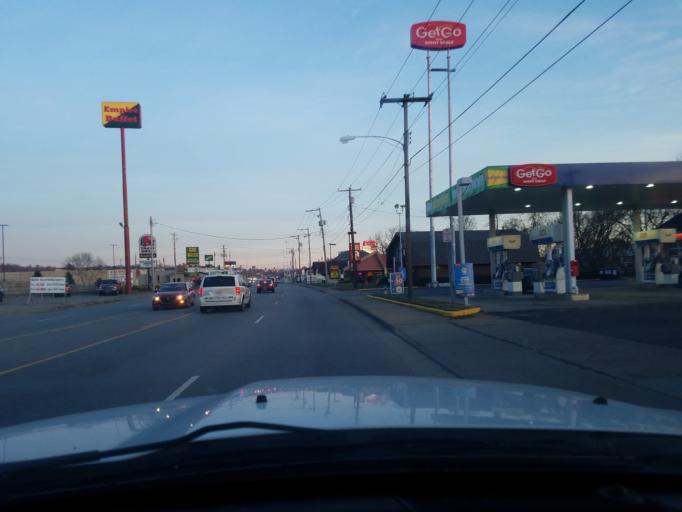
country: US
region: West Virginia
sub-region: Wood County
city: Williamstown
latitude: 39.4120
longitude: -81.4352
